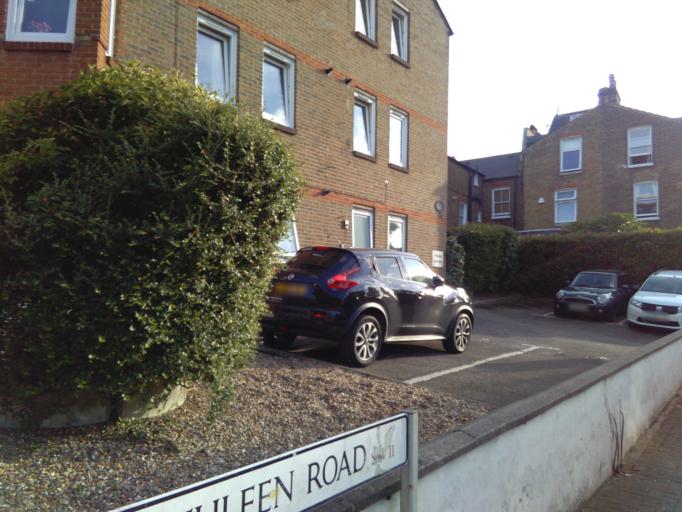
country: GB
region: England
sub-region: Greater London
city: Battersea
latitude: 51.4658
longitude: -0.1623
